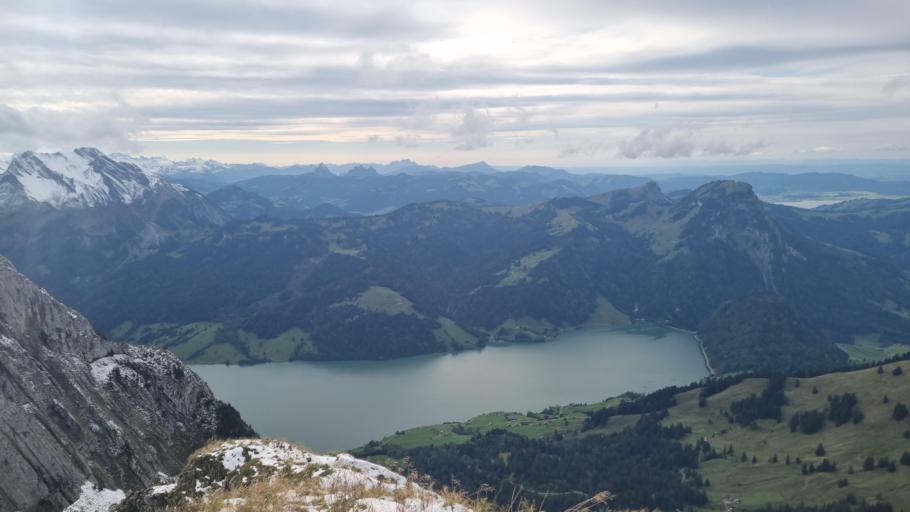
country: CH
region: Schwyz
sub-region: Bezirk March
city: Vorderthal
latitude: 47.1009
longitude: 8.9578
